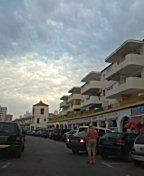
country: ES
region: Murcia
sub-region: Murcia
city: La Manga del Mar Menor
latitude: 37.6727
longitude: -0.7309
